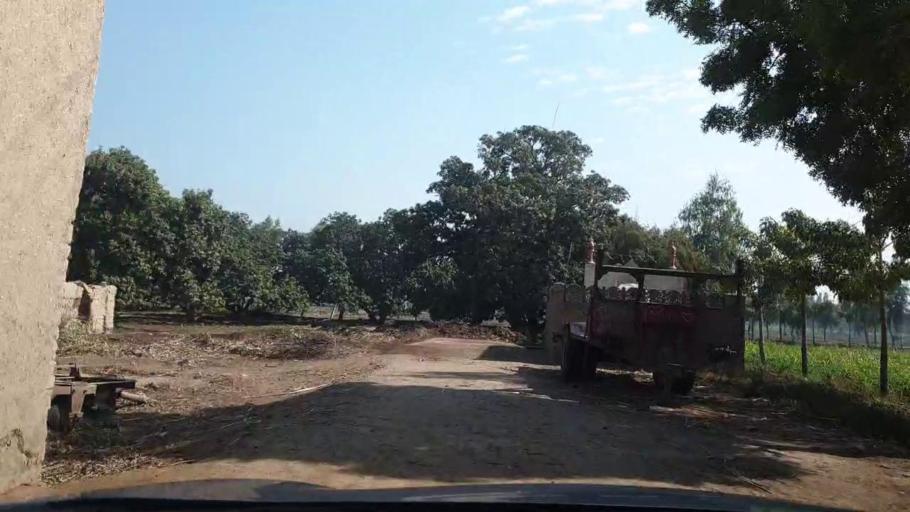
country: PK
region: Sindh
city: Tando Allahyar
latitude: 25.4752
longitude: 68.6553
